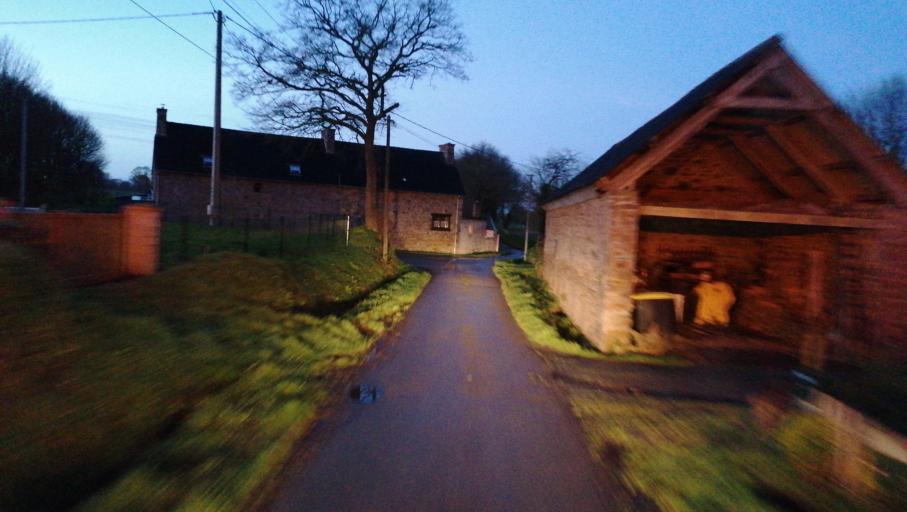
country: FR
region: Brittany
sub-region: Departement des Cotes-d'Armor
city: Lanvollon
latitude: 48.6620
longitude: -2.9679
